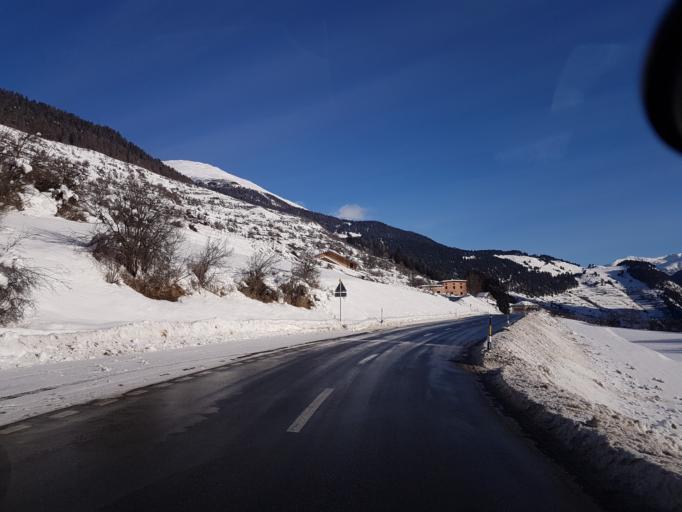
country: CH
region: Grisons
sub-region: Inn District
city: Scuol
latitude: 46.8179
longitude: 10.3577
